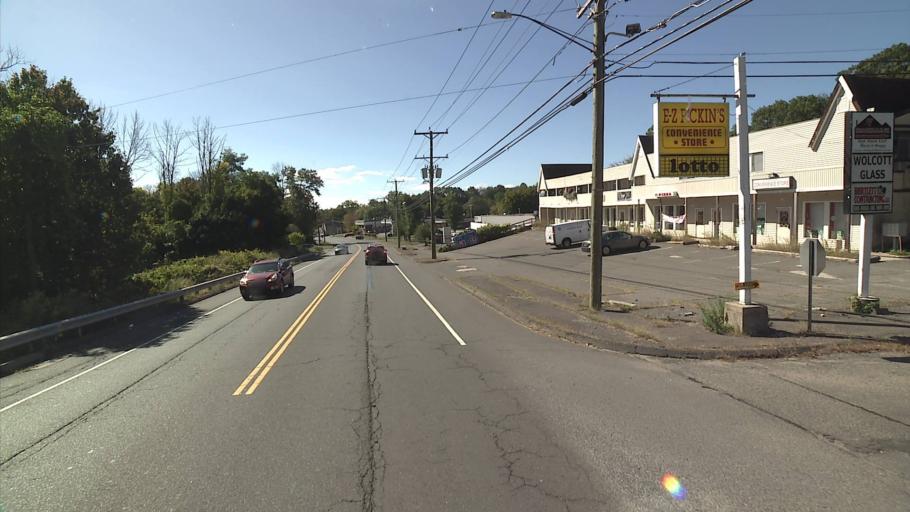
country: US
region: Connecticut
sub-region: New Haven County
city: Wolcott
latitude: 41.6035
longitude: -72.9865
